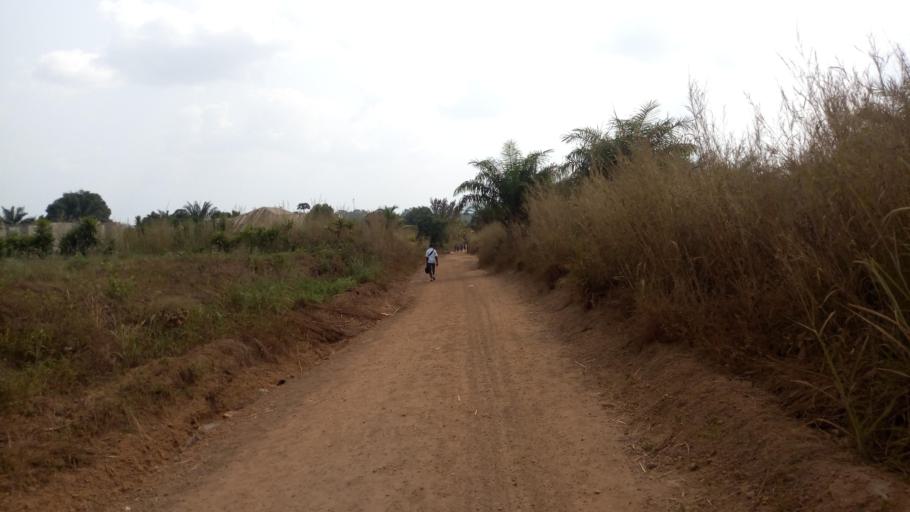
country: SL
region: Southern Province
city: Mogbwemo
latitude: 7.7773
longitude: -12.2985
